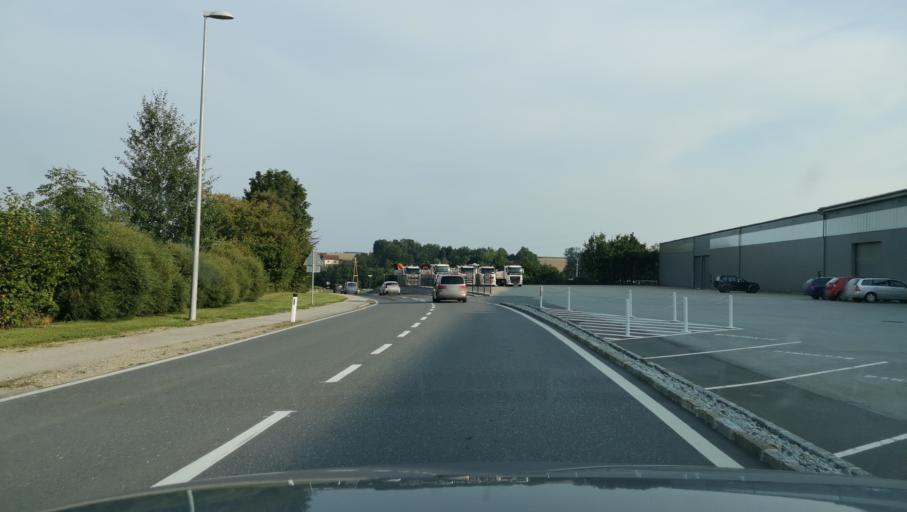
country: AT
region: Upper Austria
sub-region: Politischer Bezirk Grieskirchen
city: Grieskirchen
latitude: 48.3240
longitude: 13.7736
